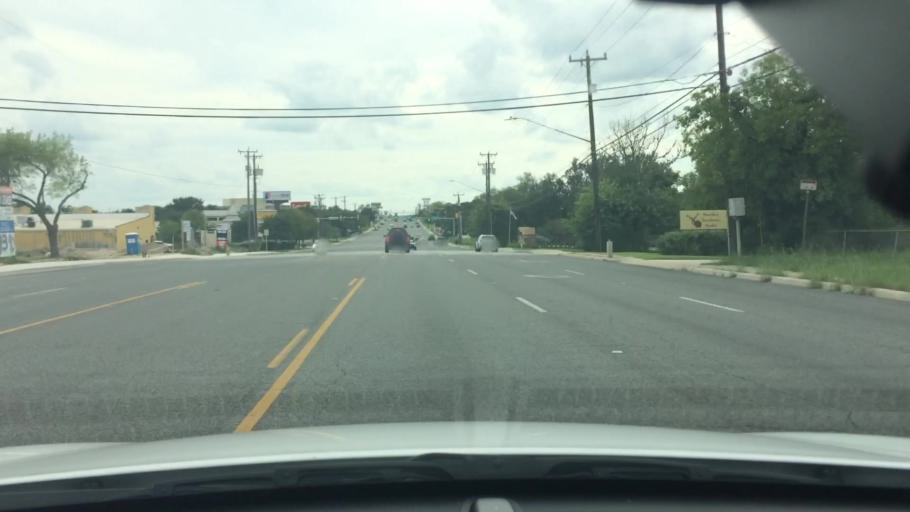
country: US
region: Texas
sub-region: Bexar County
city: Leon Valley
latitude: 29.5308
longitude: -98.5928
